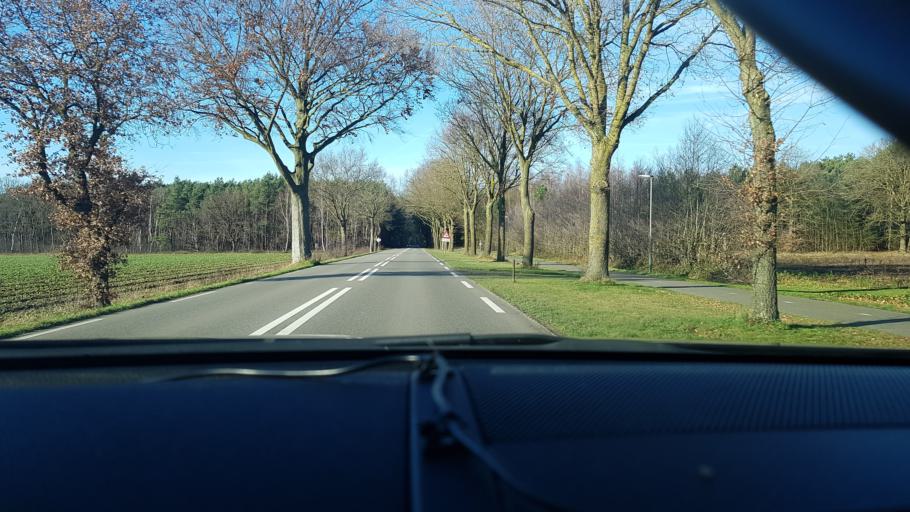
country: NL
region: Limburg
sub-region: Gemeente Beesel
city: Beesel
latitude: 51.3046
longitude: 6.0263
